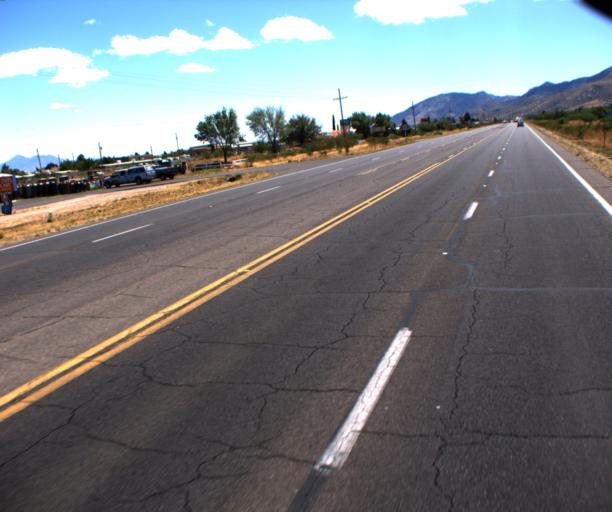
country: US
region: Arizona
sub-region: Cochise County
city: Sierra Vista Southeast
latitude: 31.4886
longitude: -110.2575
